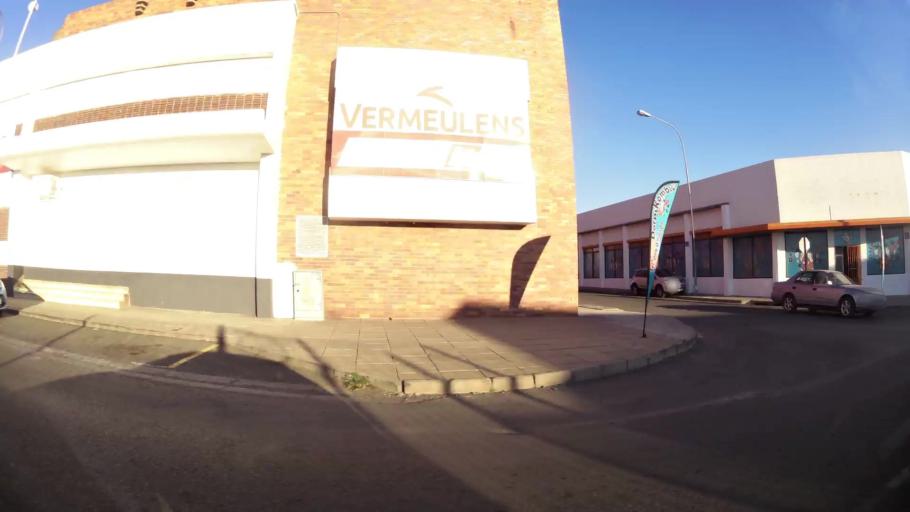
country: ZA
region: Northern Cape
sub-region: Frances Baard District Municipality
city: Kimberley
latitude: -28.7418
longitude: 24.7600
